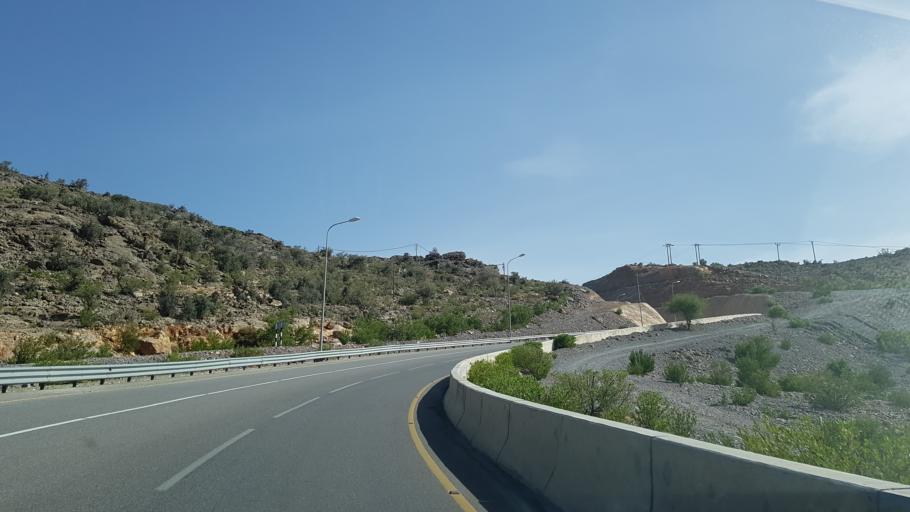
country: OM
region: Muhafazat ad Dakhiliyah
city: Izki
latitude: 23.0780
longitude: 57.7036
